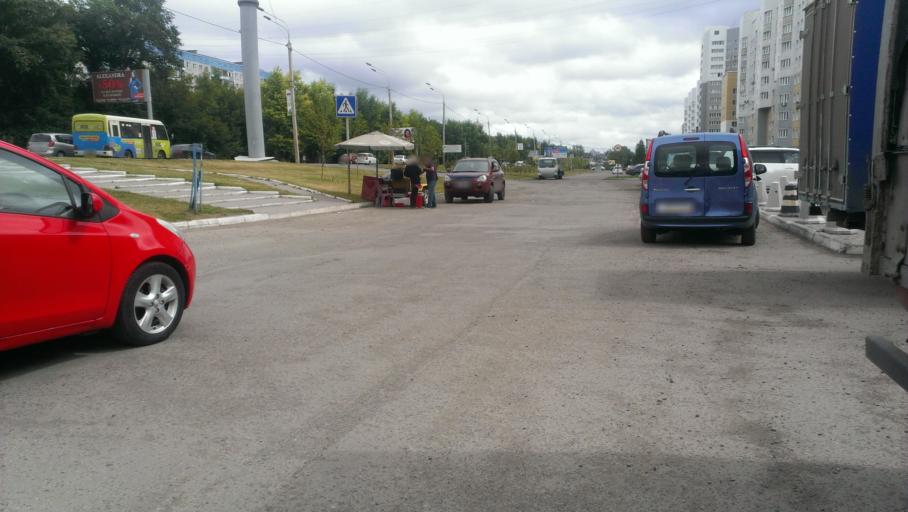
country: RU
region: Altai Krai
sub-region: Gorod Barnaulskiy
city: Barnaul
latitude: 53.3410
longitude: 83.7053
